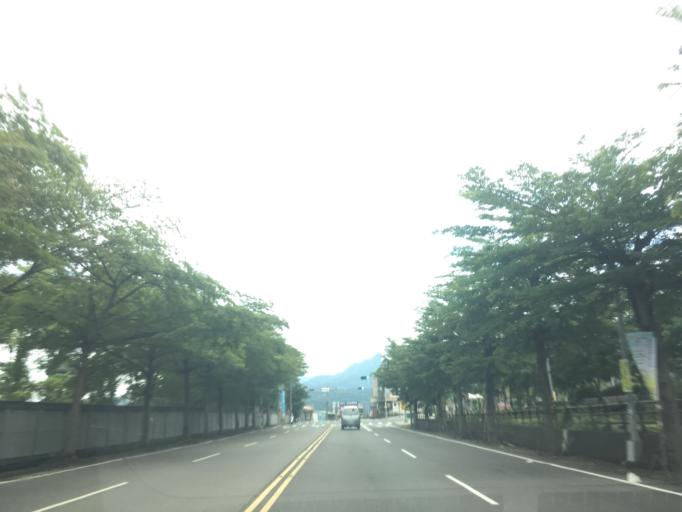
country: TW
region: Taiwan
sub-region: Yunlin
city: Douliu
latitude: 23.5928
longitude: 120.5308
